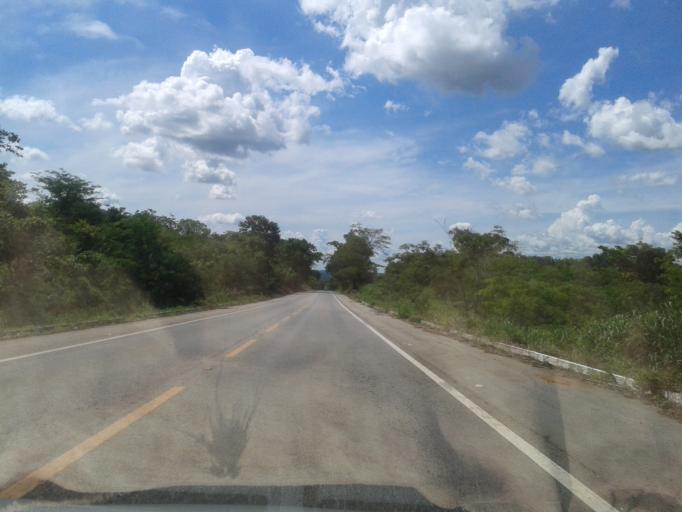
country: BR
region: Goias
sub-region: Goias
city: Goias
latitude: -15.7741
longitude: -50.1423
